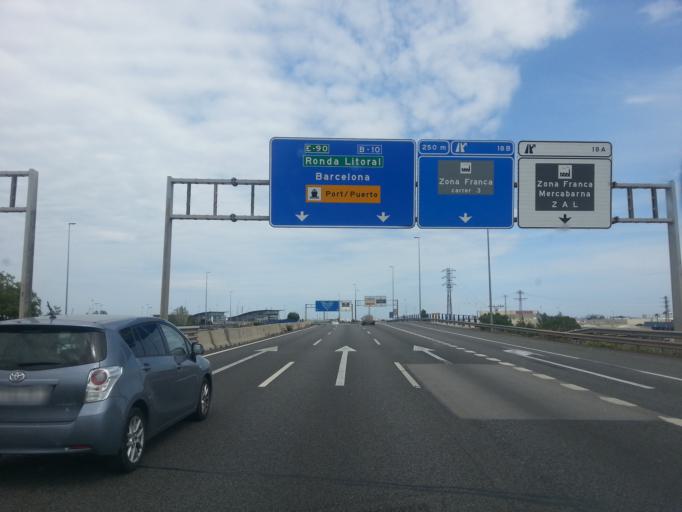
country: ES
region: Catalonia
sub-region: Provincia de Barcelona
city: El Prat de Llobregat
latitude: 41.3399
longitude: 2.1134
